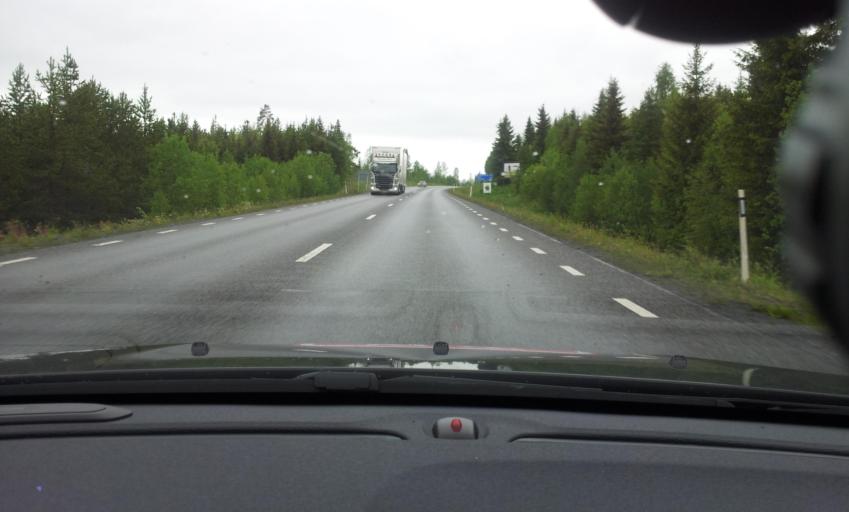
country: SE
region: Jaemtland
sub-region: Krokoms Kommun
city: Valla
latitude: 63.3067
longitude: 13.9138
